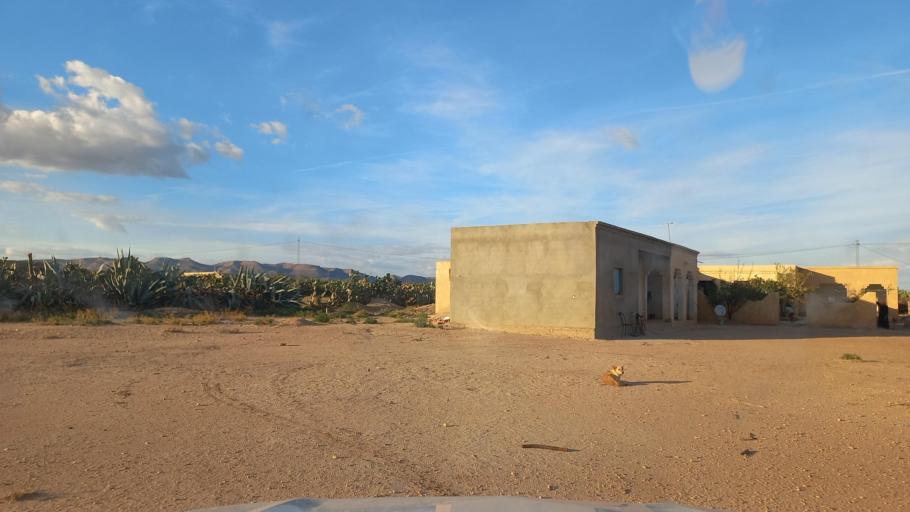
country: TN
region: Al Qasrayn
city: Sbiba
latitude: 35.3530
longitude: 9.0345
